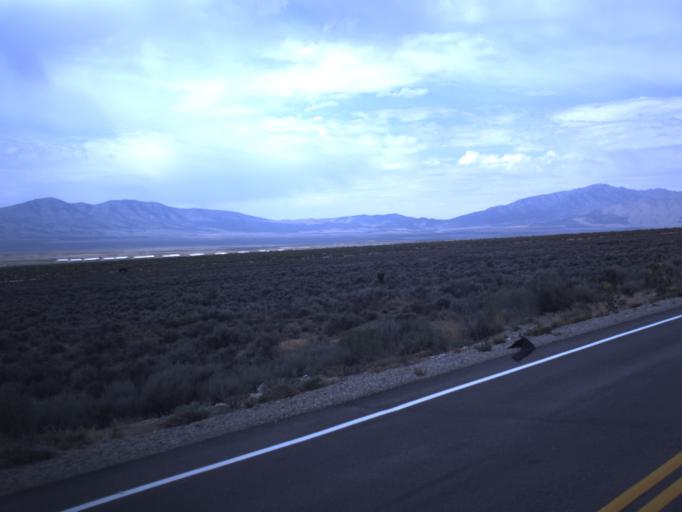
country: US
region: Utah
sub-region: Tooele County
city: Tooele
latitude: 40.2884
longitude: -112.2679
